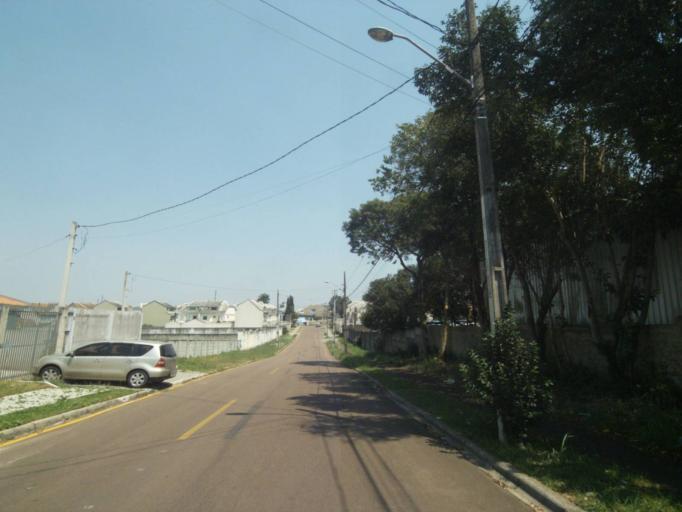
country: BR
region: Parana
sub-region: Sao Jose Dos Pinhais
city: Sao Jose dos Pinhais
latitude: -25.4993
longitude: -49.2688
